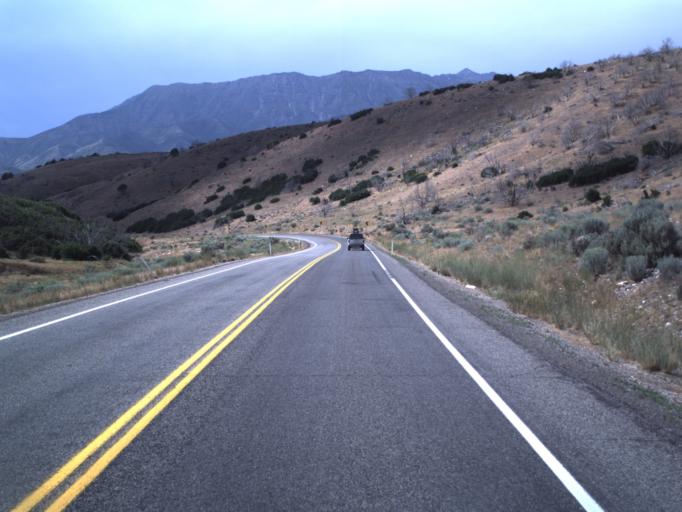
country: US
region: Utah
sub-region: Sanpete County
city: Fountain Green
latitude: 39.7000
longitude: -111.6985
